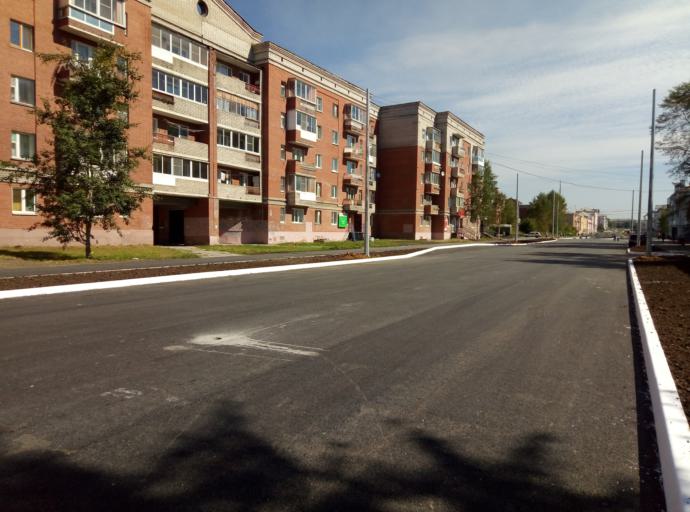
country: RU
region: Sverdlovsk
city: Krasnotur'insk
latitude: 59.7637
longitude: 60.1817
